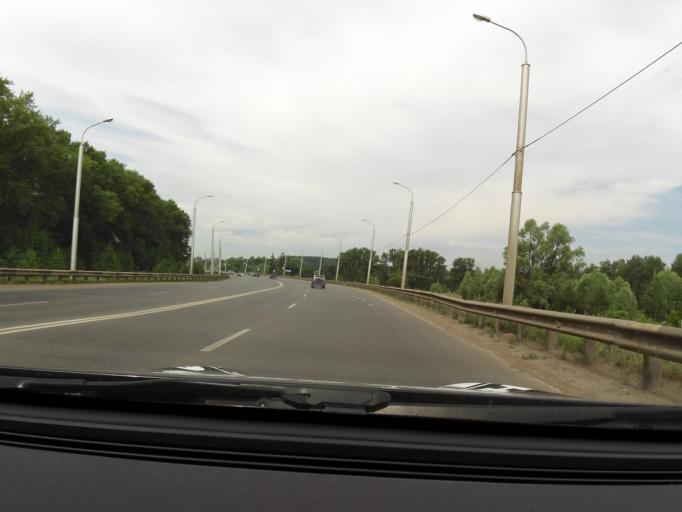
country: RU
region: Bashkortostan
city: Ufa
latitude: 54.8088
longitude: 56.1683
